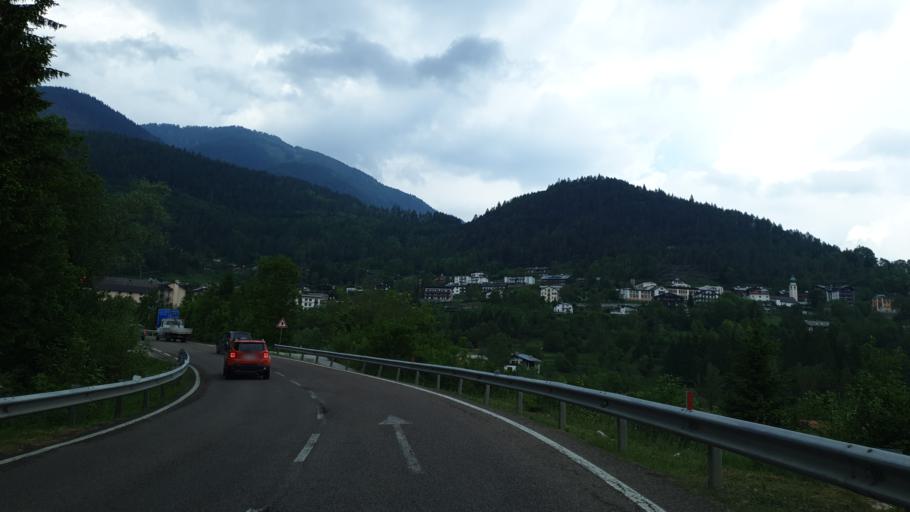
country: IT
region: Veneto
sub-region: Provincia di Belluno
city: Pieve di Cadore
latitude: 46.4212
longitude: 12.3674
